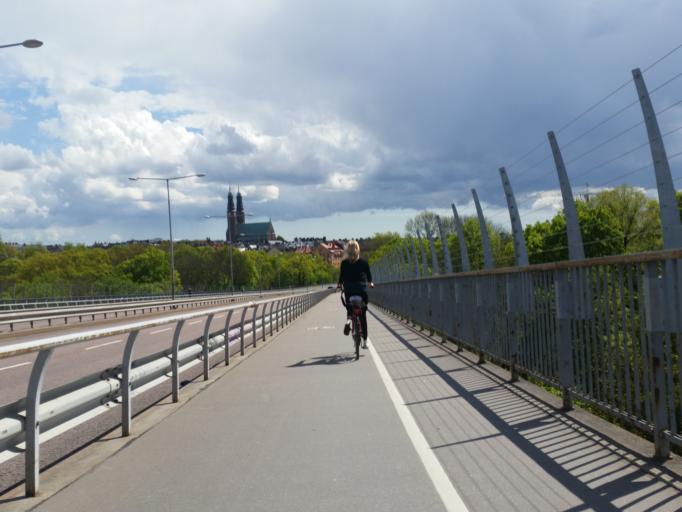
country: SE
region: Stockholm
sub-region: Stockholms Kommun
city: Arsta
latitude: 59.3232
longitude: 18.0285
